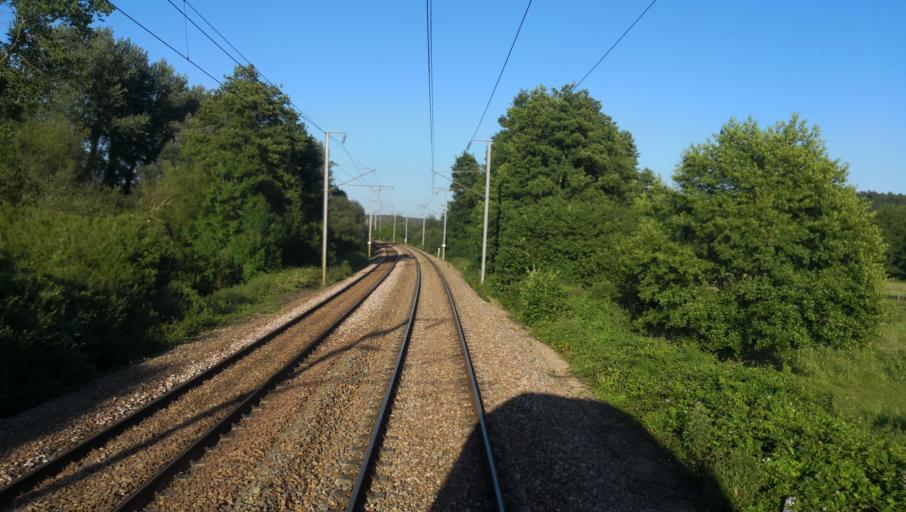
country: FR
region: Haute-Normandie
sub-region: Departement de l'Eure
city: Menneval
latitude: 49.0896
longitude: 0.6562
